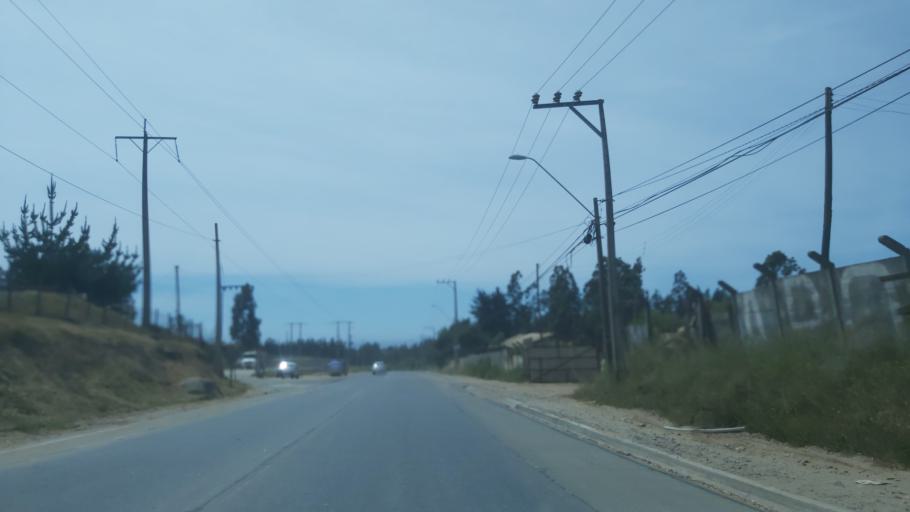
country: CL
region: Maule
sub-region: Provincia de Talca
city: Constitucion
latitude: -35.3617
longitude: -72.4048
